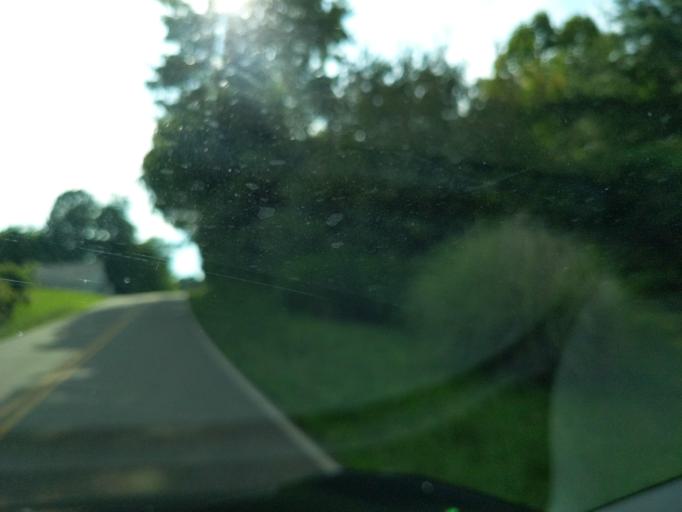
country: US
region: Ohio
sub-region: Fairfield County
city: Lancaster
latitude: 39.5613
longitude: -82.6113
